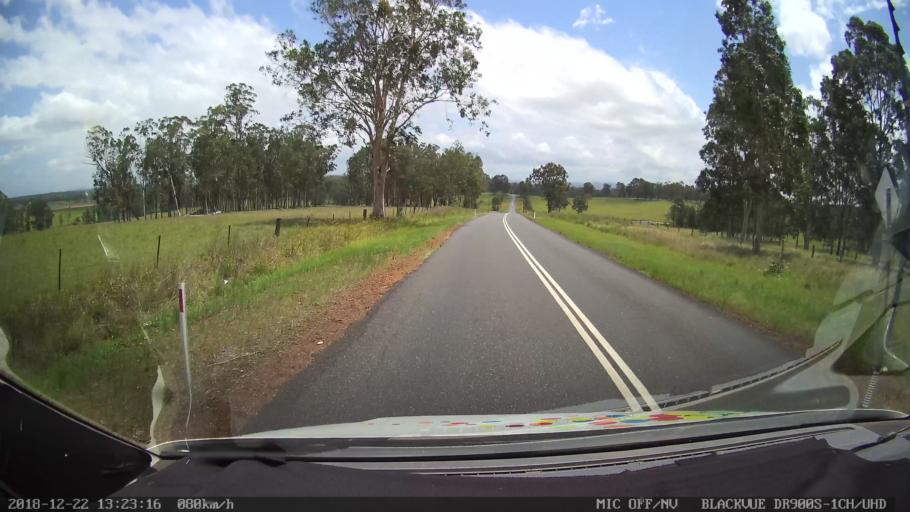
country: AU
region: New South Wales
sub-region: Clarence Valley
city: Coutts Crossing
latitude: -29.7961
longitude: 152.9085
